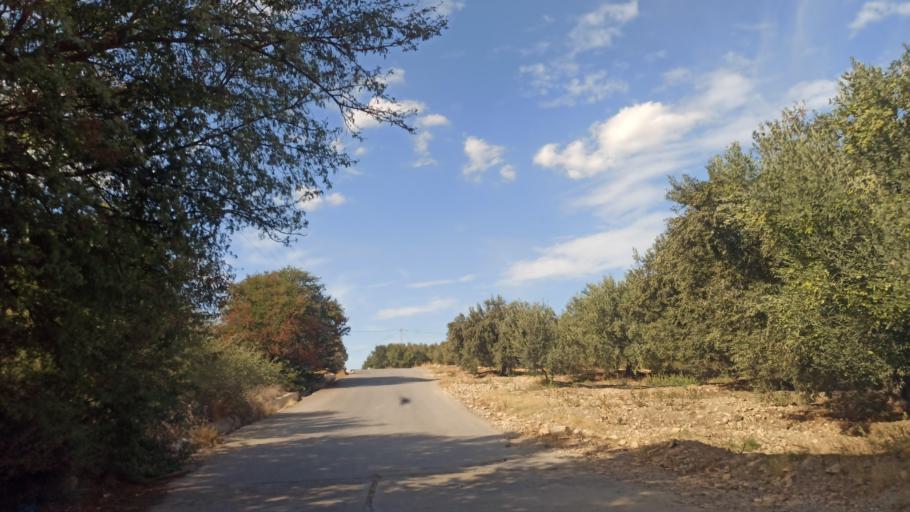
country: TN
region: Zaghwan
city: Zaghouan
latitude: 36.3341
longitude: 10.2123
